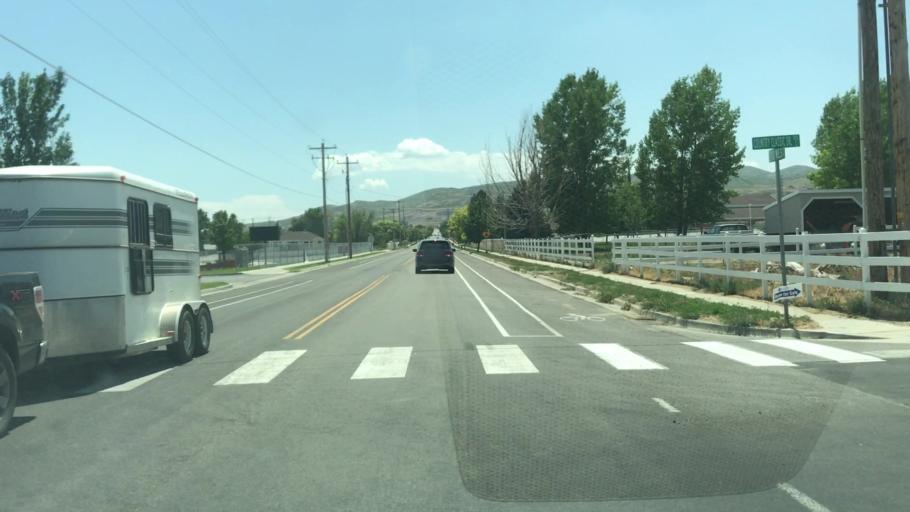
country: US
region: Utah
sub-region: Salt Lake County
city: Bluffdale
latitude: 40.4922
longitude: -111.9578
